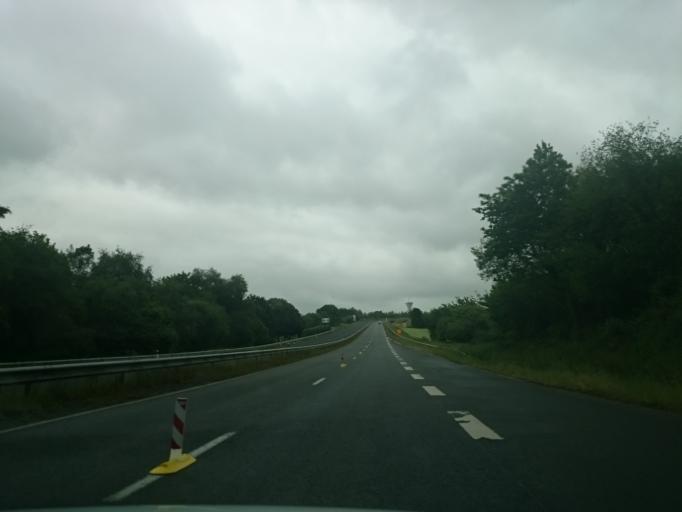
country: FR
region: Brittany
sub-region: Departement des Cotes-d'Armor
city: Begard
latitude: 48.6155
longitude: -3.2844
